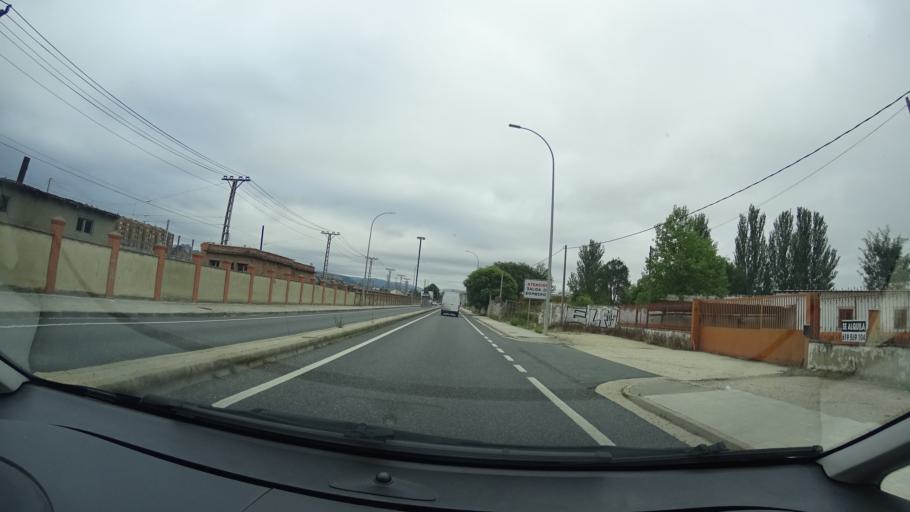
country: ES
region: Castille and Leon
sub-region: Provincia de Burgos
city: Miranda de Ebro
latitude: 42.6924
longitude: -2.9406
